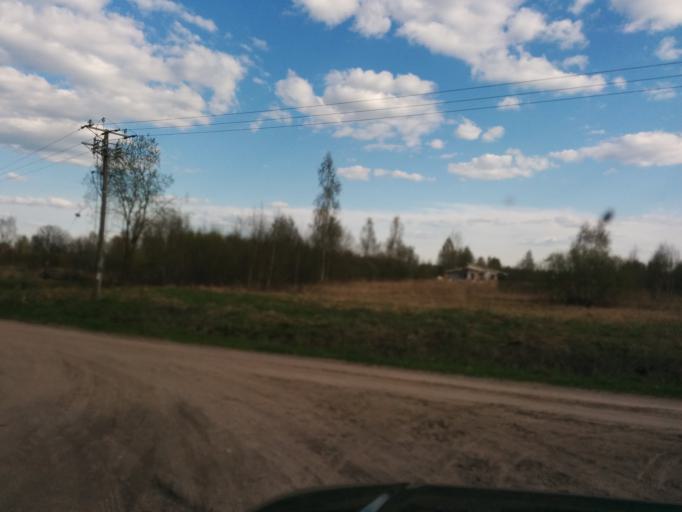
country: LV
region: Jelgava
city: Jelgava
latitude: 56.6689
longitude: 23.6562
